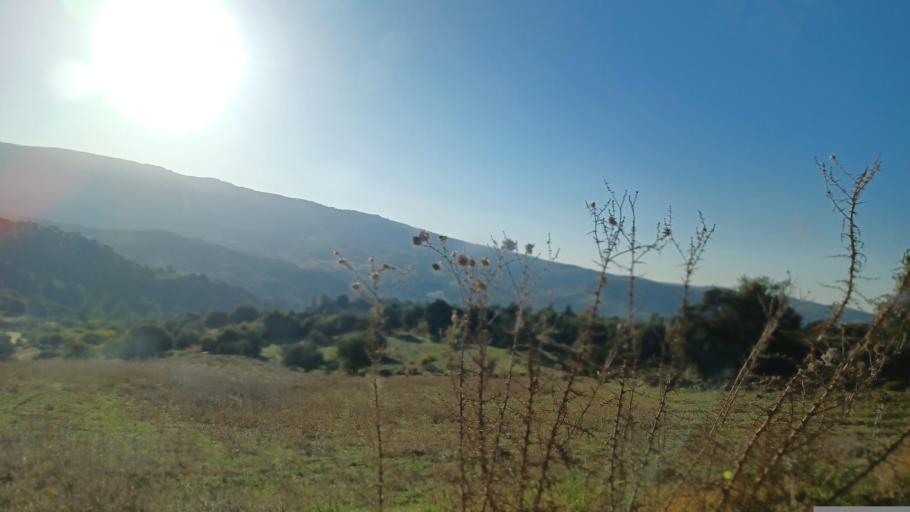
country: CY
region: Pafos
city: Mesogi
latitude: 34.9312
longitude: 32.5664
